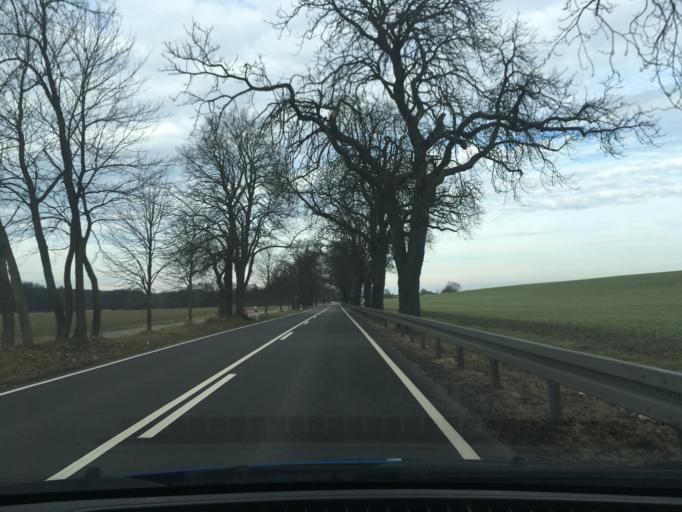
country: DE
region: Mecklenburg-Vorpommern
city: Boizenburg
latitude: 53.4169
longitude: 10.7437
